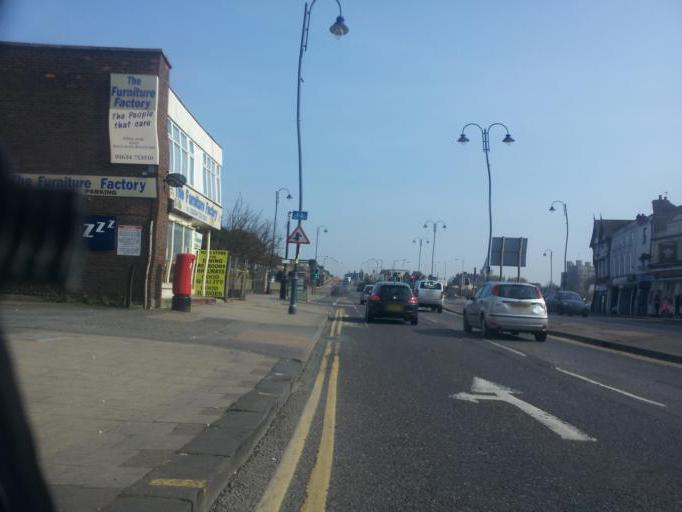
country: GB
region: England
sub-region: Kent
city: Strood
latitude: 51.3943
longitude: 0.4979
